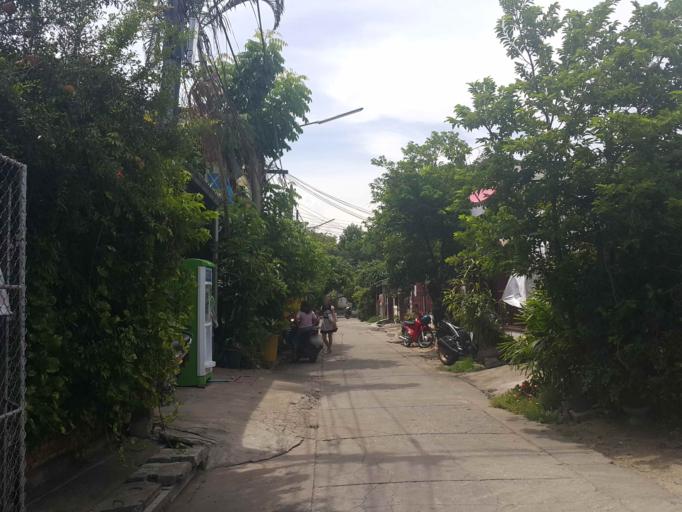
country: TH
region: Chiang Mai
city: Chiang Mai
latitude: 18.7622
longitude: 99.0120
